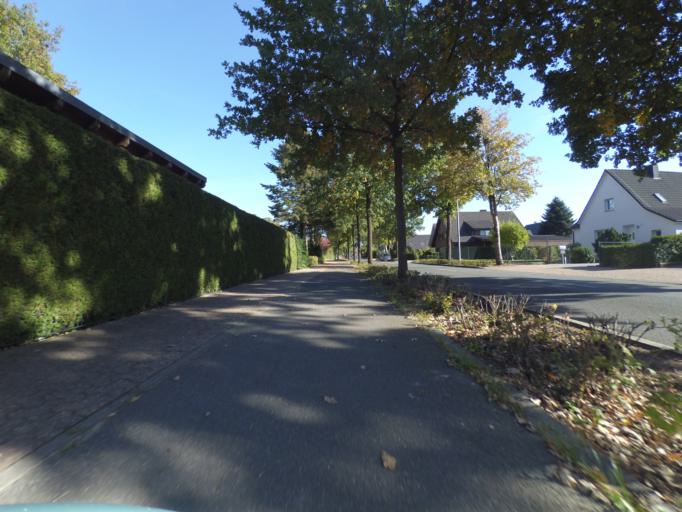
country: DE
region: North Rhine-Westphalia
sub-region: Regierungsbezirk Dusseldorf
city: Bocholt
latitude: 51.8876
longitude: 6.6576
